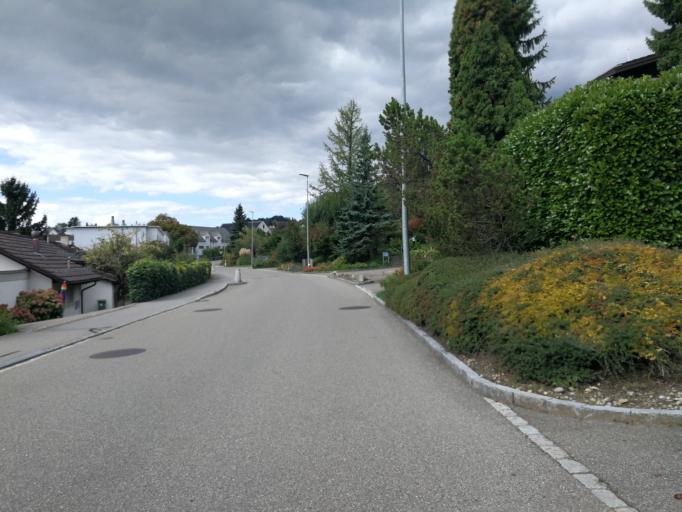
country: CH
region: Zurich
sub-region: Bezirk Meilen
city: Stafa
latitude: 47.2461
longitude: 8.7290
